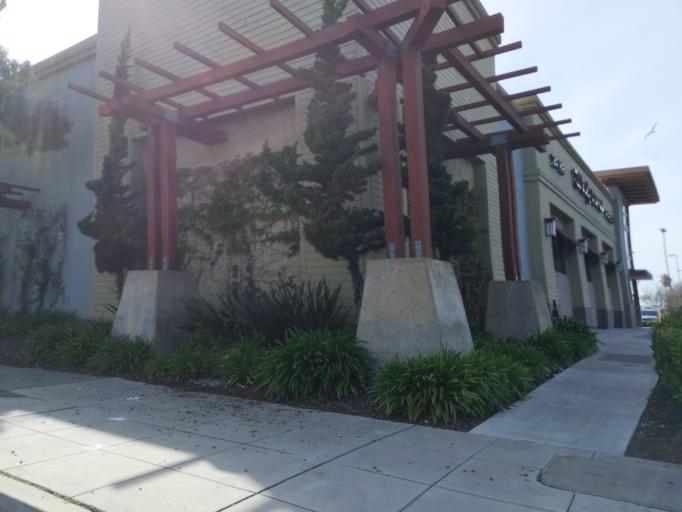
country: US
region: California
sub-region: Alameda County
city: Alameda
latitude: 37.7573
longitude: -122.2488
